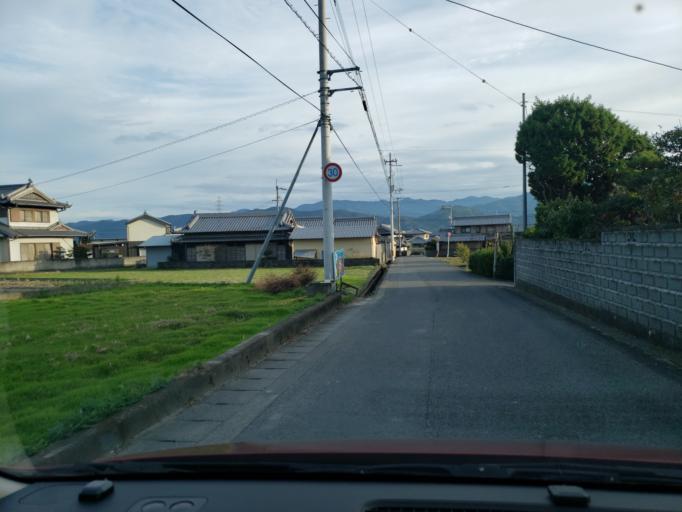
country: JP
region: Tokushima
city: Wakimachi
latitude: 34.0820
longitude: 134.2277
